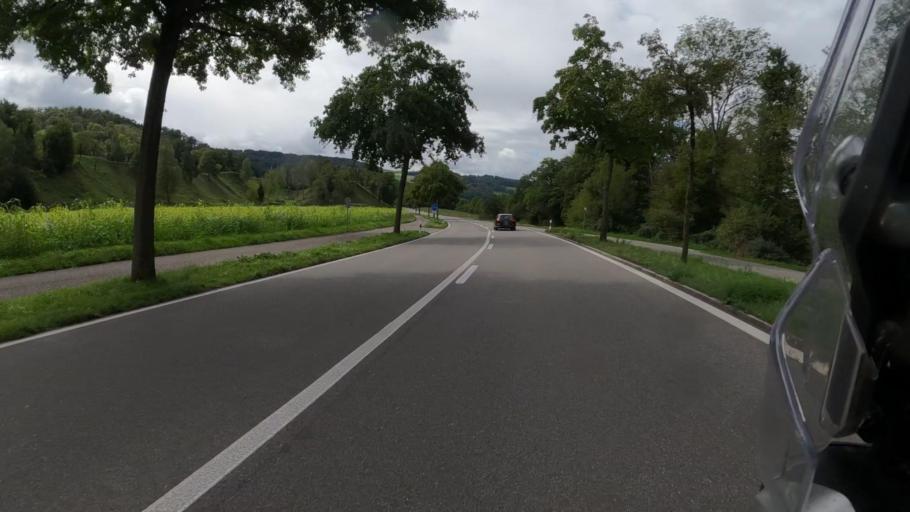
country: DE
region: Baden-Wuerttemberg
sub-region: Freiburg Region
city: Hohentengen am Hochrhein
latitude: 47.5746
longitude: 8.3939
